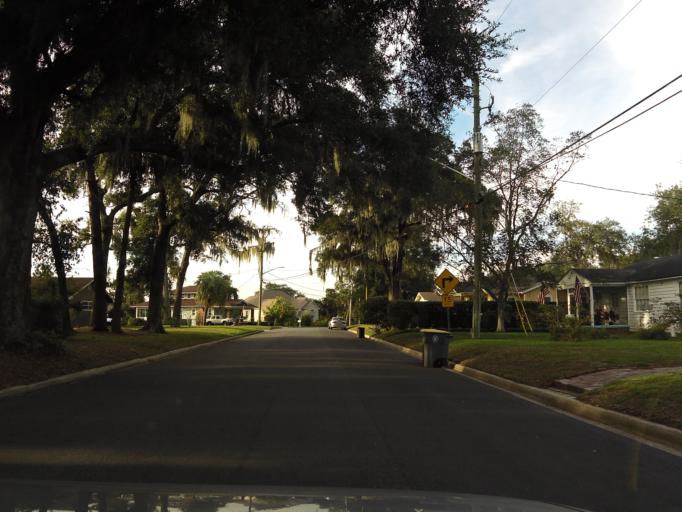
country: US
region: Florida
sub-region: Duval County
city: Jacksonville
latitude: 30.3868
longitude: -81.6628
